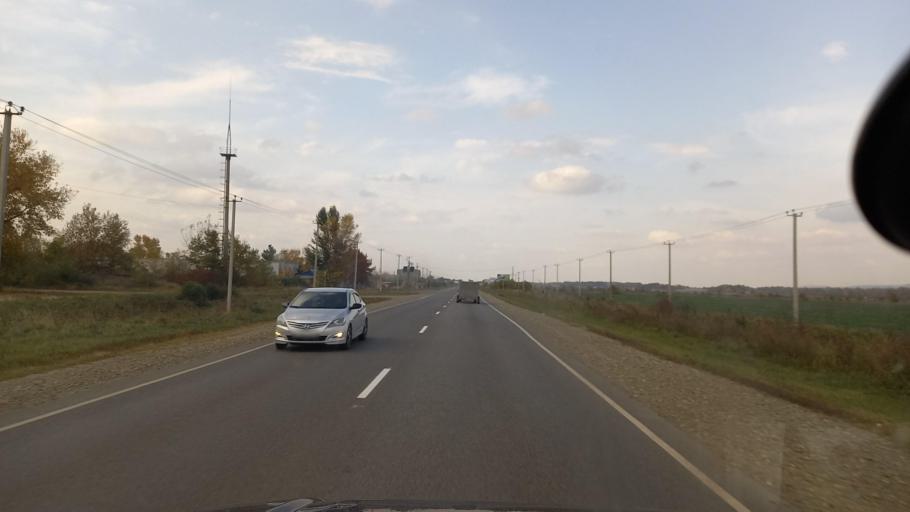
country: RU
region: Krasnodarskiy
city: Mostovskoy
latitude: 44.3803
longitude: 40.8217
